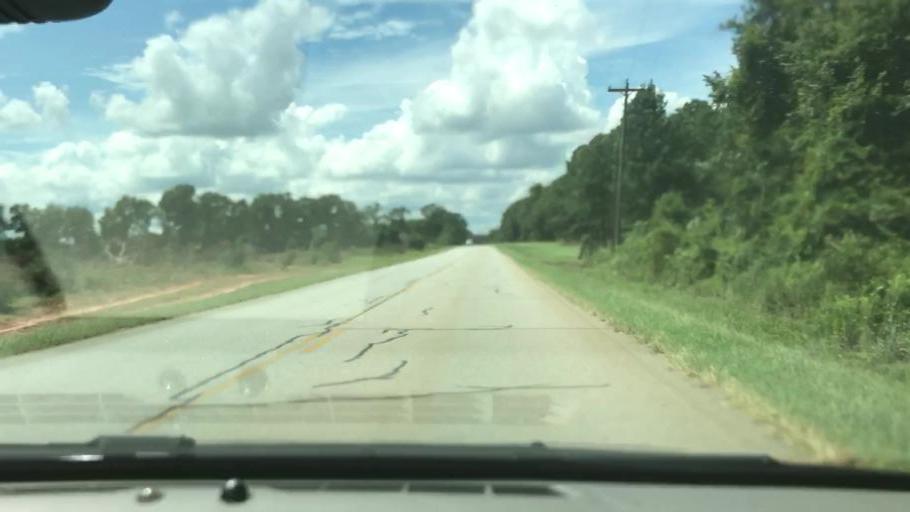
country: US
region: Georgia
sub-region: Stewart County
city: Lumpkin
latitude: 32.1370
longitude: -84.9735
